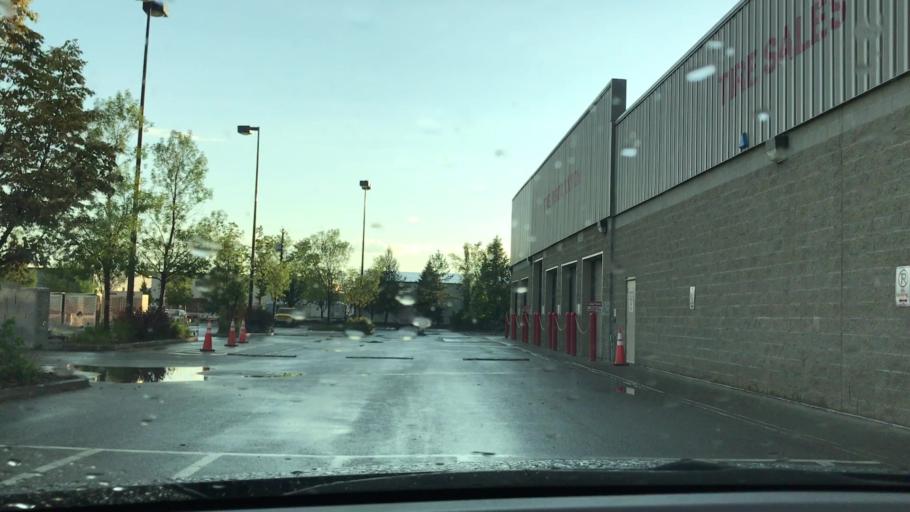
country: CA
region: Alberta
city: Edmonton
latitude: 53.4551
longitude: -113.4693
